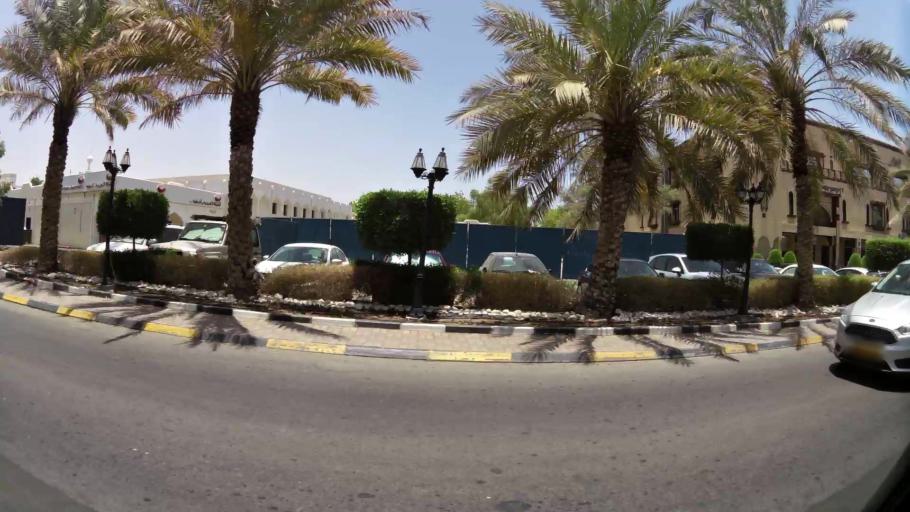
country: OM
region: Muhafazat Masqat
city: Bawshar
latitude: 23.6000
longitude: 58.4559
